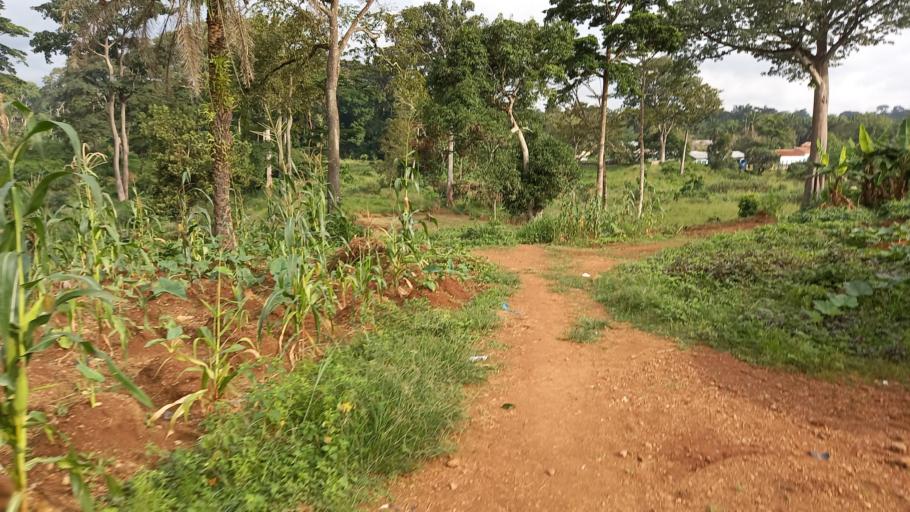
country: SL
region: Eastern Province
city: Kailahun
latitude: 8.2794
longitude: -10.5784
